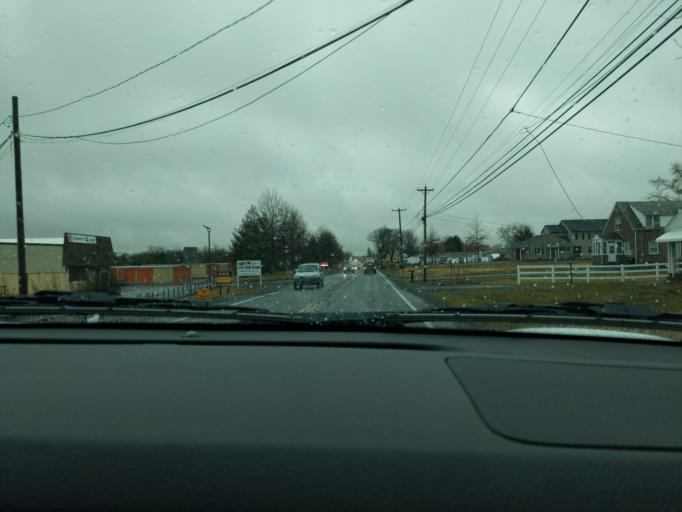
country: US
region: Pennsylvania
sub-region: Bucks County
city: Dublin
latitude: 40.3788
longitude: -75.2141
